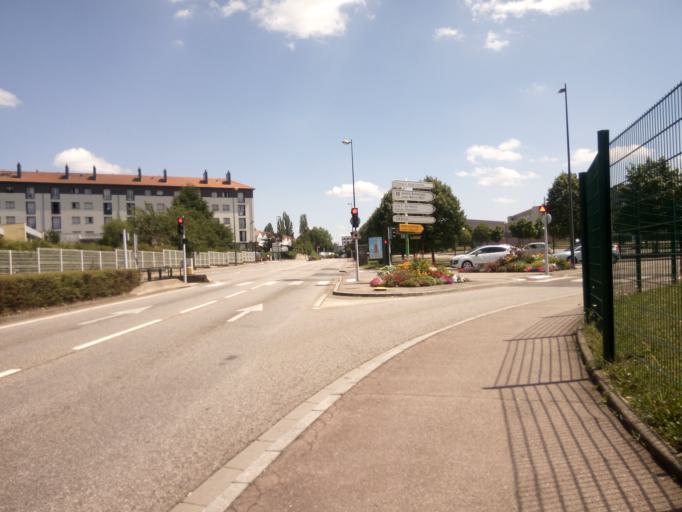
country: FR
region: Lorraine
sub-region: Departement de Meurthe-et-Moselle
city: Villers-les-Nancy
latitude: 48.6690
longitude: 6.1606
